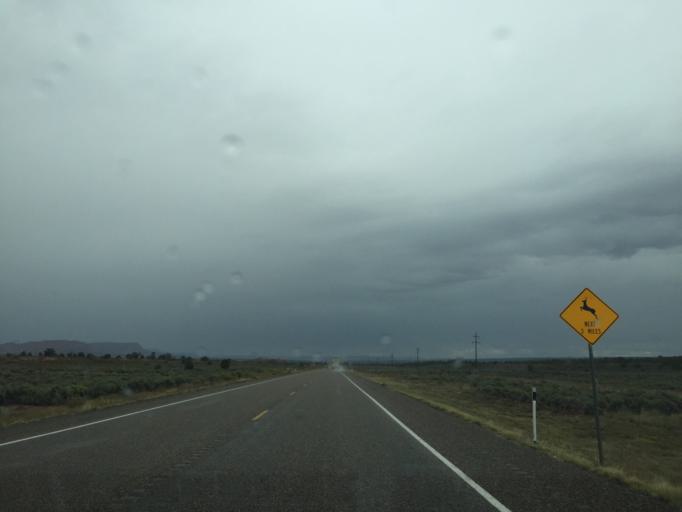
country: US
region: Utah
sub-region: Kane County
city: Kanab
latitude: 37.0946
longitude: -112.1409
